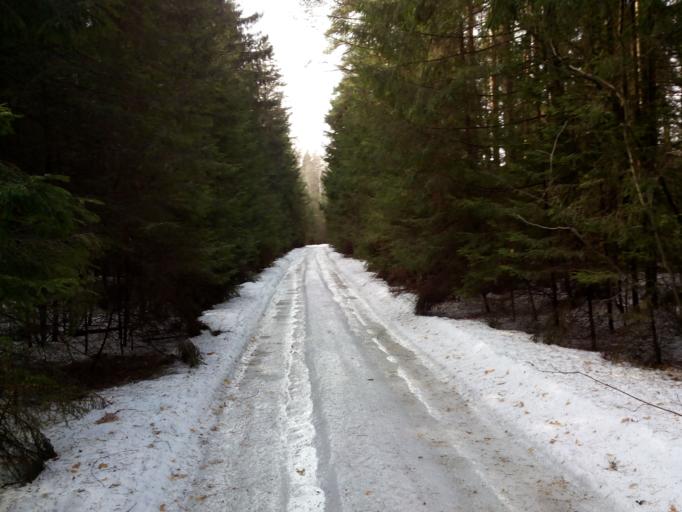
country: RU
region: Moskovskaya
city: Zhukovka
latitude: 56.4855
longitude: 37.5675
